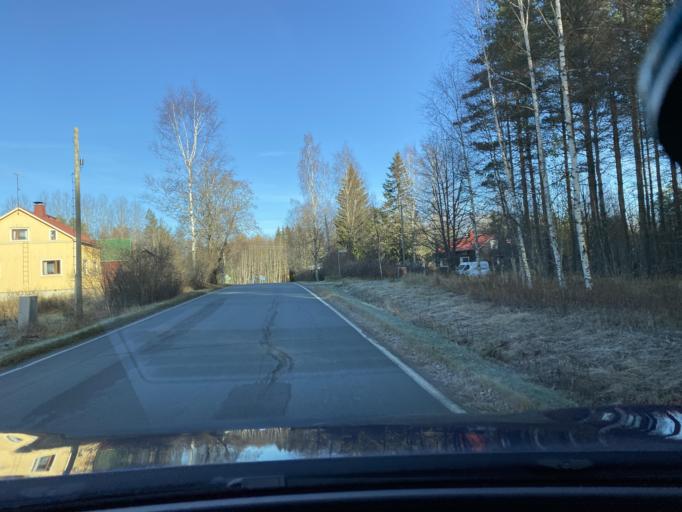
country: FI
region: Haeme
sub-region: Forssa
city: Tammela
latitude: 60.9081
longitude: 23.8613
